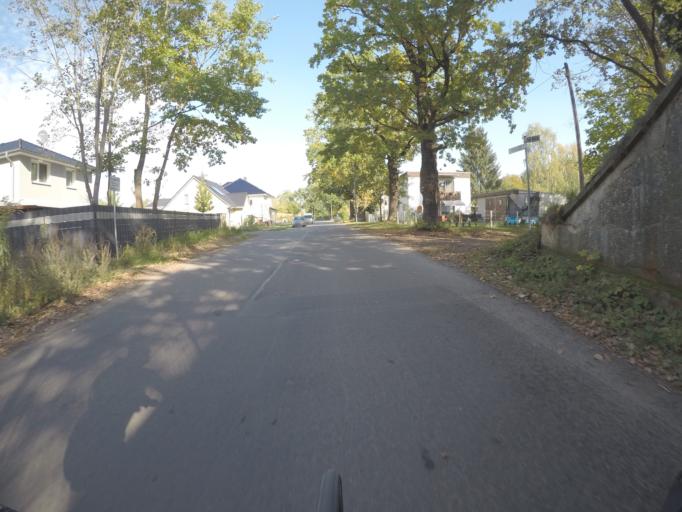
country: DE
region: Brandenburg
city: Oranienburg
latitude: 52.7419
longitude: 13.2247
